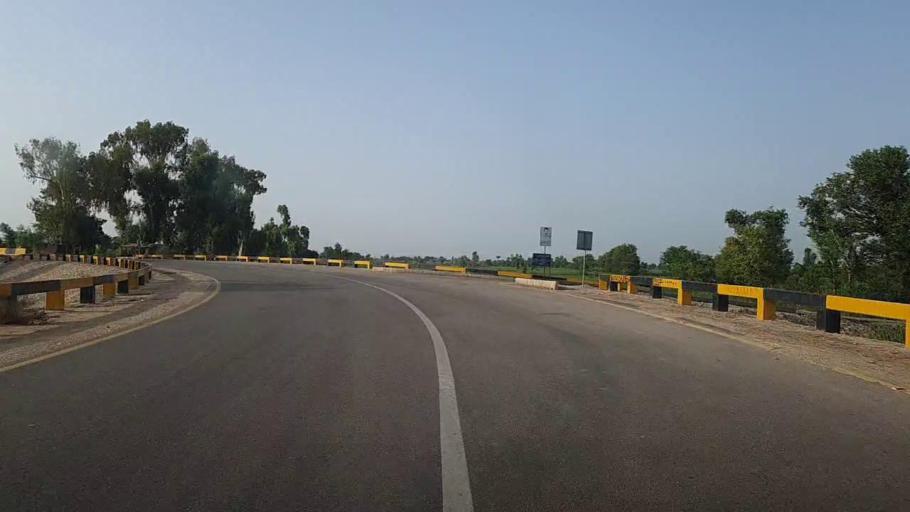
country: PK
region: Sindh
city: Naushahro Firoz
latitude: 26.7925
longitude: 68.1448
